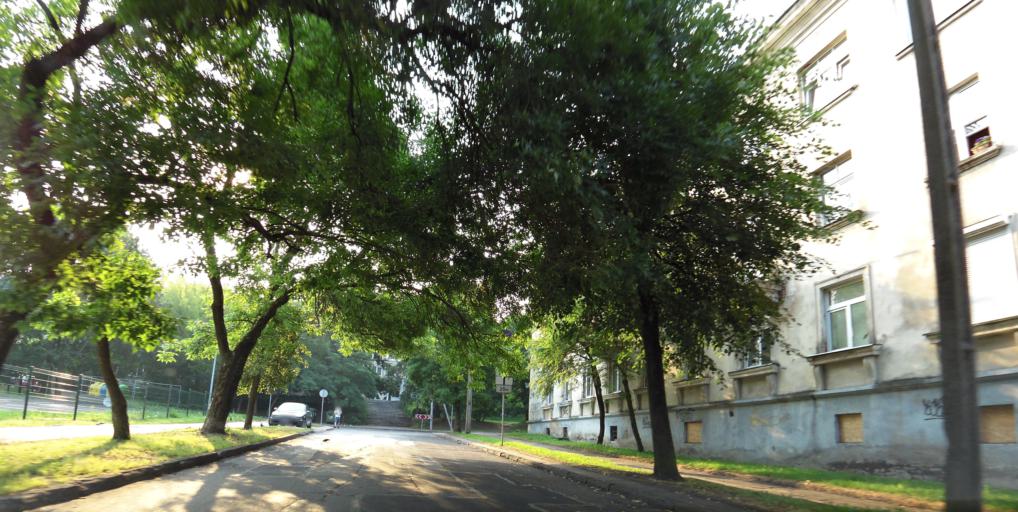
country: LT
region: Vilnius County
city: Rasos
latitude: 54.7078
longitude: 25.3174
